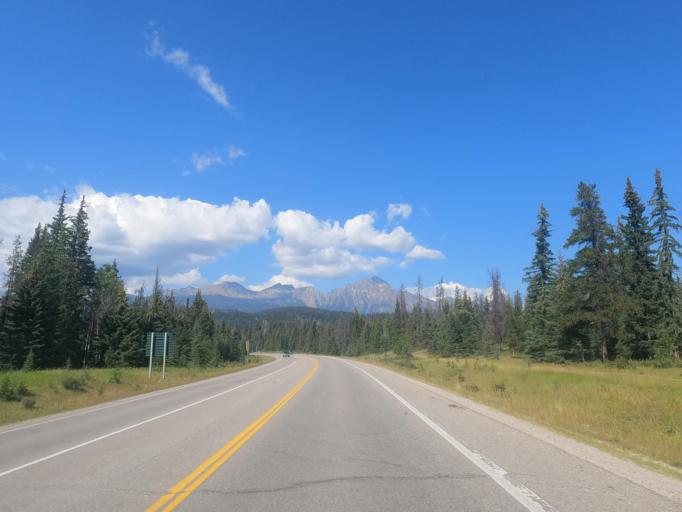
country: CA
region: Alberta
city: Jasper Park Lodge
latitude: 52.8589
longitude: -118.0798
